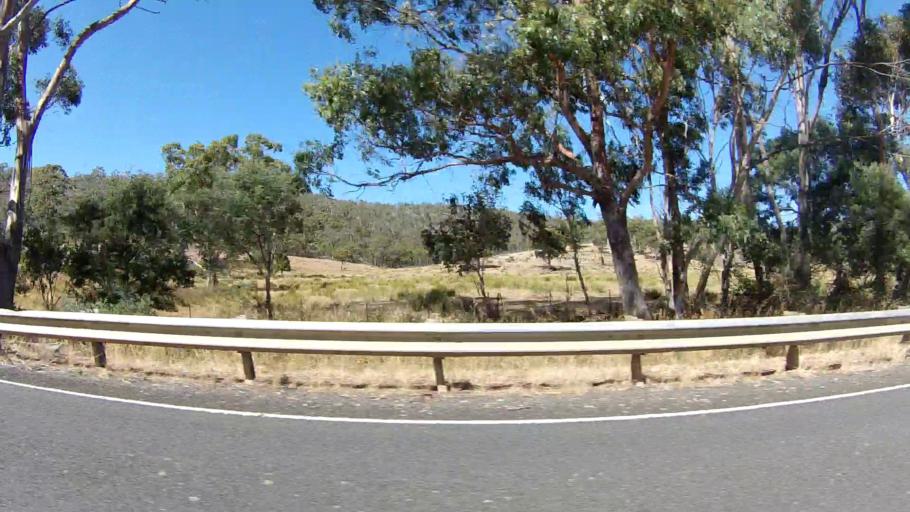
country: AU
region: Tasmania
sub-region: Sorell
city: Sorell
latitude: -42.5916
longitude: 147.7968
